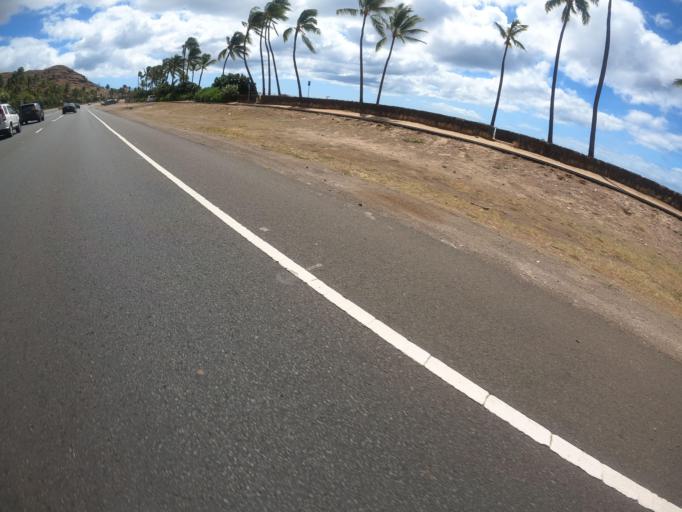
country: US
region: Hawaii
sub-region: Honolulu County
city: Nanakuli
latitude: 21.3575
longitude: -158.1304
